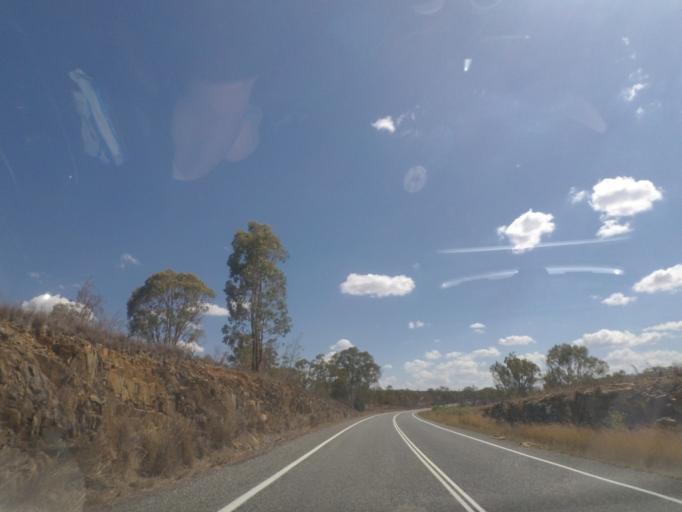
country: AU
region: Queensland
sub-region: Southern Downs
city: Warwick
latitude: -28.2153
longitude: 151.5628
